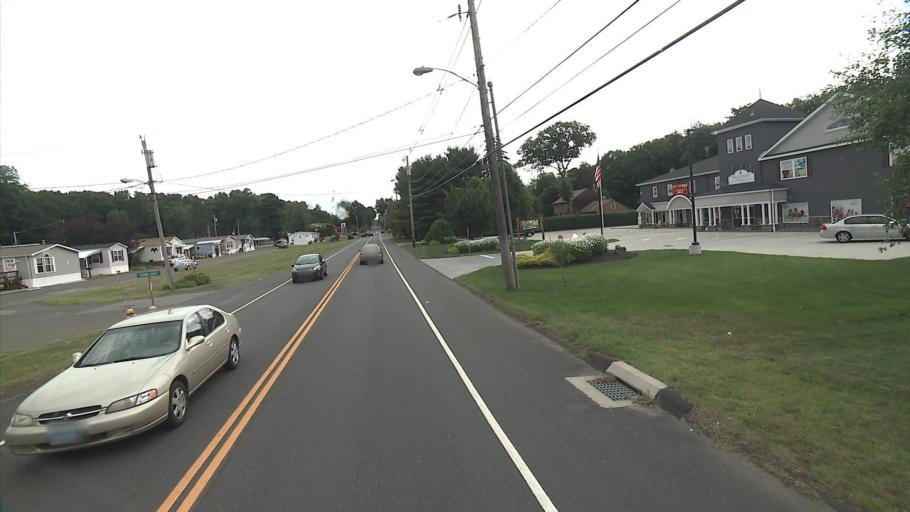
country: US
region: Connecticut
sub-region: New Haven County
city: Wallingford
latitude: 41.4828
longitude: -72.8253
